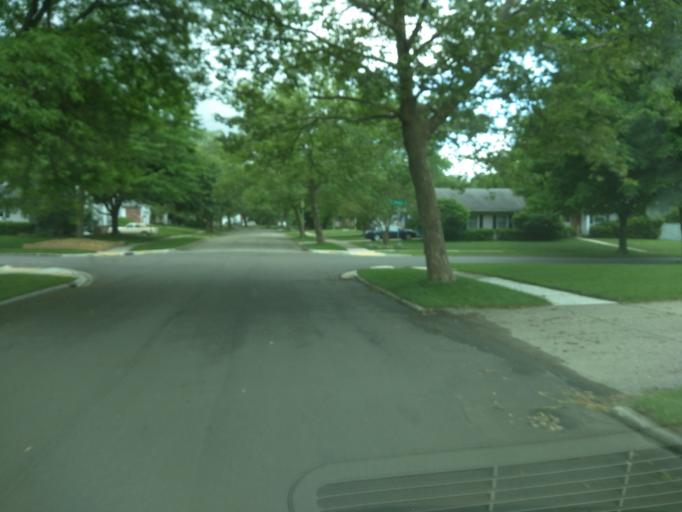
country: US
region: Michigan
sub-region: Eaton County
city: Waverly
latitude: 42.7043
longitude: -84.5972
